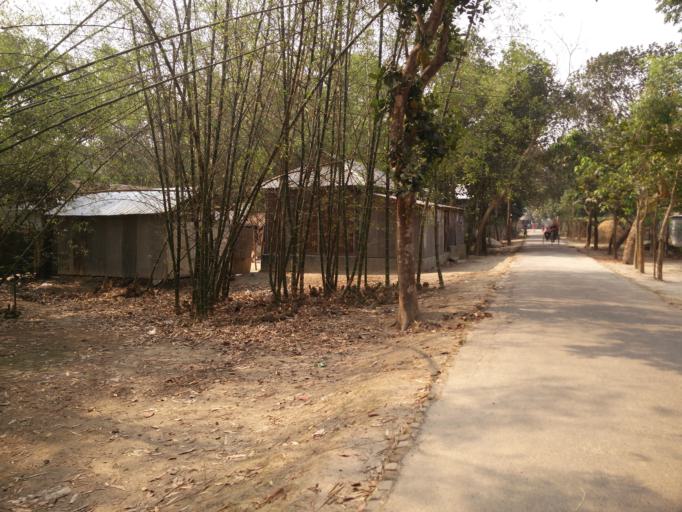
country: BD
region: Dhaka
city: Sherpur
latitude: 24.9119
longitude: 90.1560
